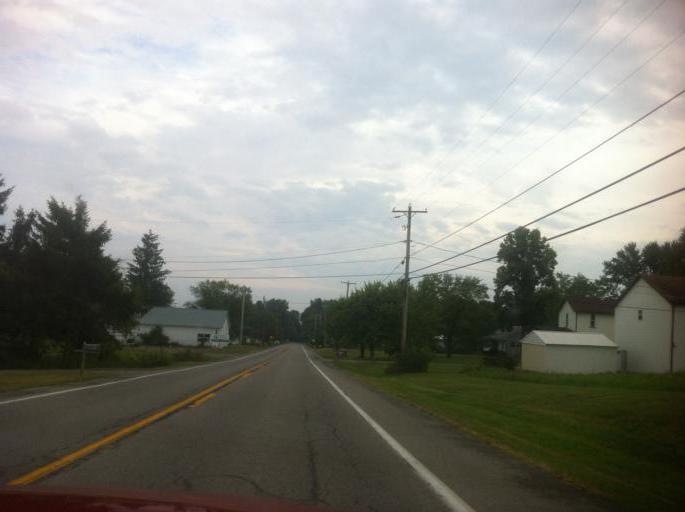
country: US
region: Pennsylvania
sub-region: Mercer County
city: Grove City
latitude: 41.1812
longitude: -80.0840
